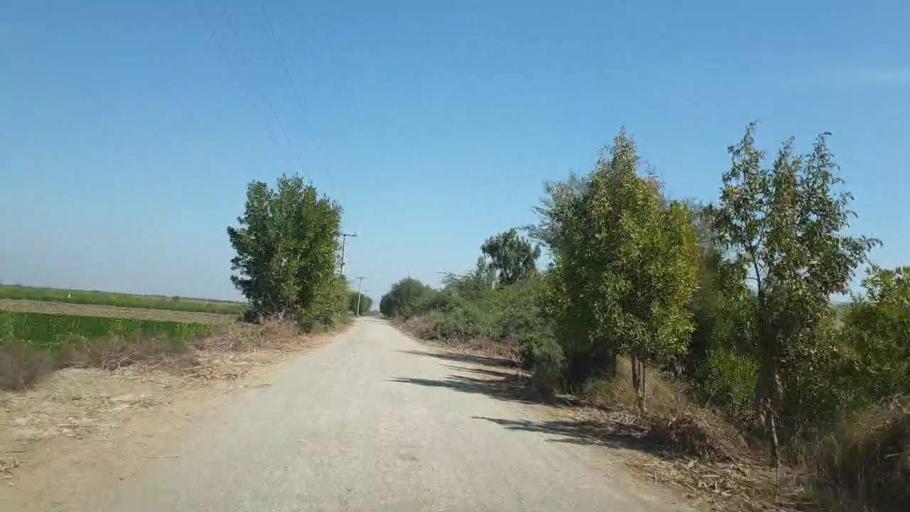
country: PK
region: Sindh
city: Mirpur Khas
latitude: 25.5998
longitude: 69.1194
